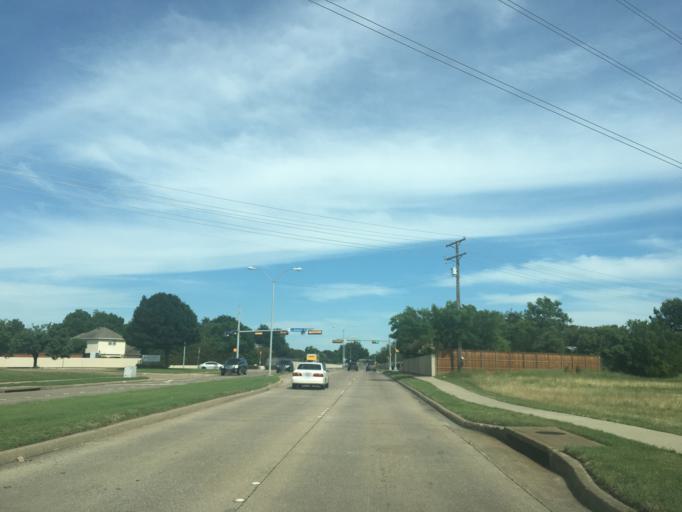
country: US
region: Texas
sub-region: Dallas County
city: Richardson
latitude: 32.9352
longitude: -96.7134
